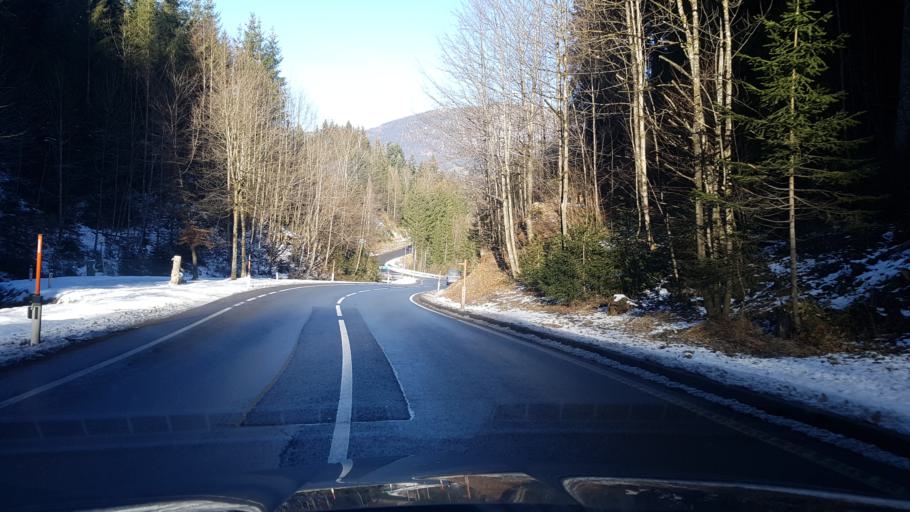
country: AT
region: Salzburg
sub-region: Politischer Bezirk Hallein
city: Abtenau
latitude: 47.5659
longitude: 13.3798
